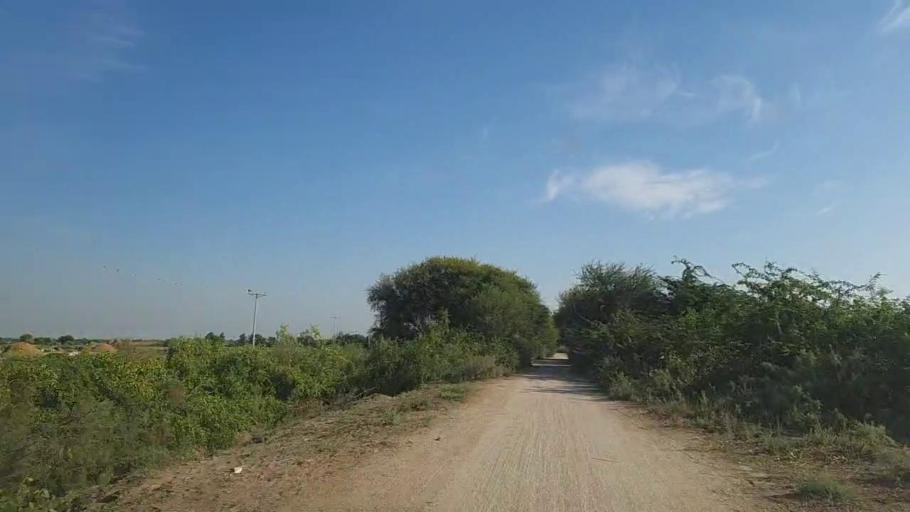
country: PK
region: Sindh
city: Bulri
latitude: 24.7797
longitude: 68.3548
